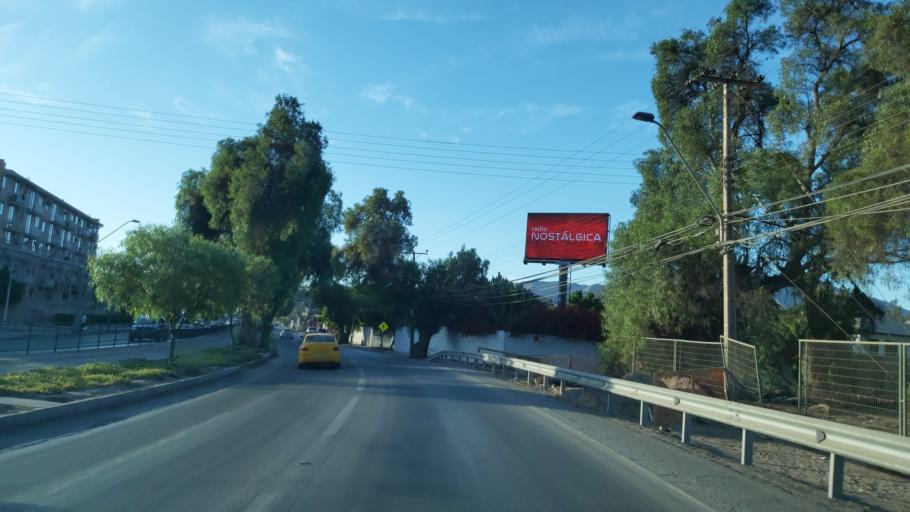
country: CL
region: Atacama
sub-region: Provincia de Copiapo
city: Copiapo
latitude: -27.3854
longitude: -70.3134
